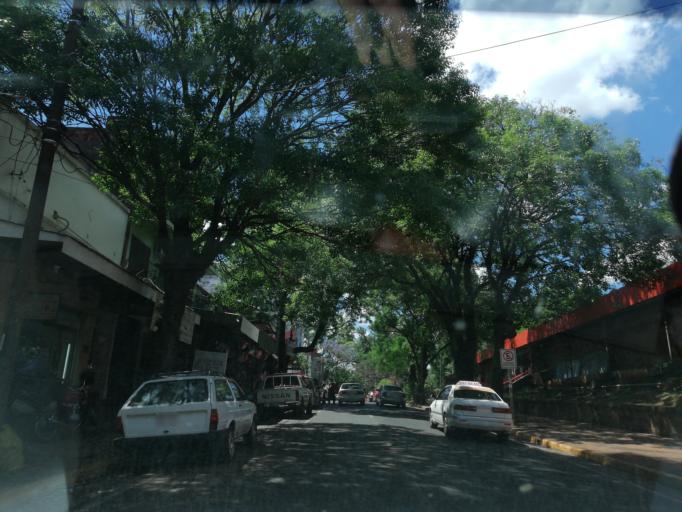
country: PY
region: Itapua
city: Encarnacion
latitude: -27.3405
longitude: -55.8657
